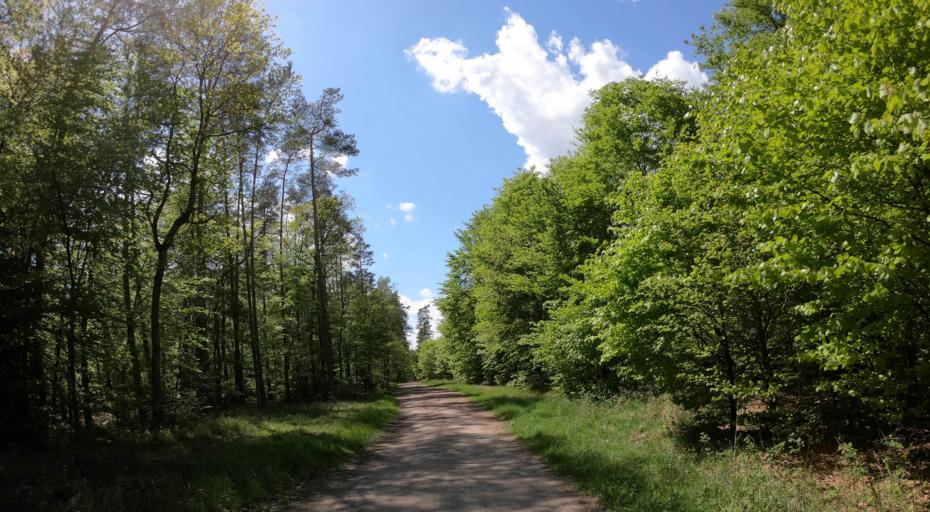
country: PL
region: West Pomeranian Voivodeship
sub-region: Powiat lobeski
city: Lobez
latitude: 53.5979
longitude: 15.6400
